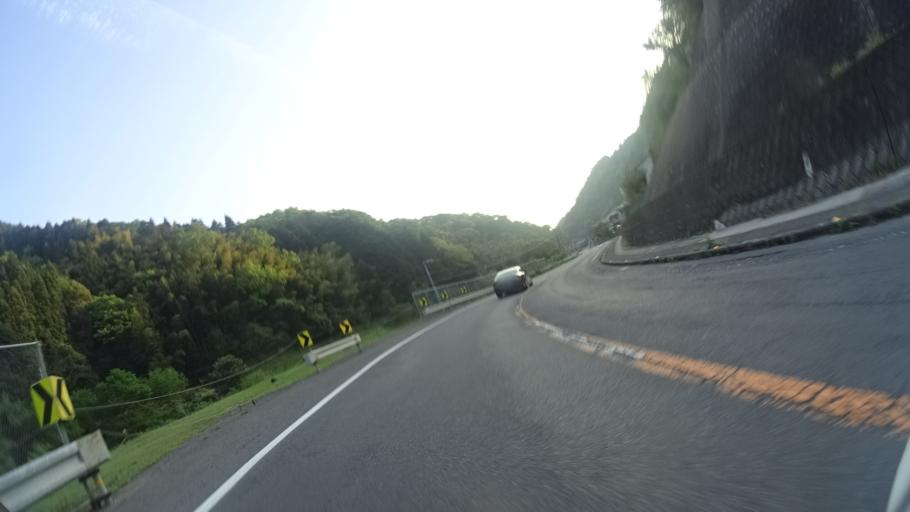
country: JP
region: Ehime
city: Kawanoecho
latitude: 33.9940
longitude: 133.6495
